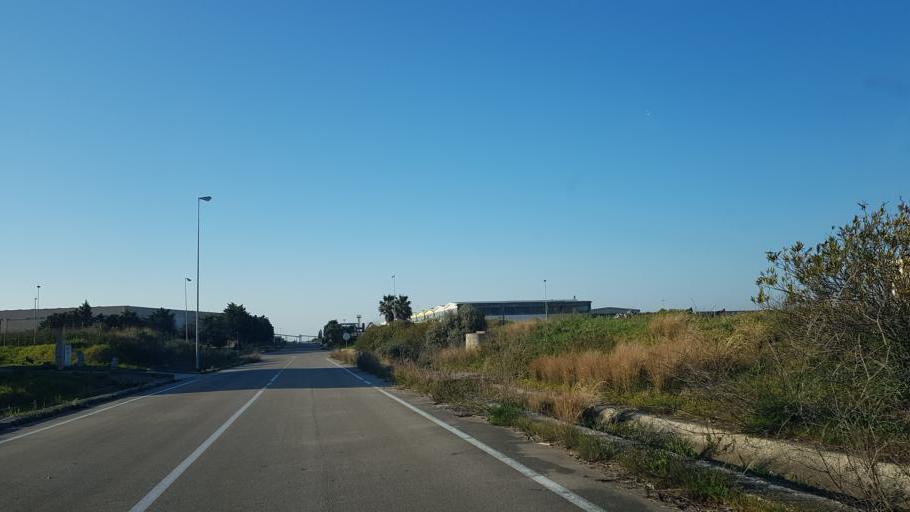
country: IT
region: Apulia
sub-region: Provincia di Brindisi
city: La Rosa
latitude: 40.6246
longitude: 17.9706
